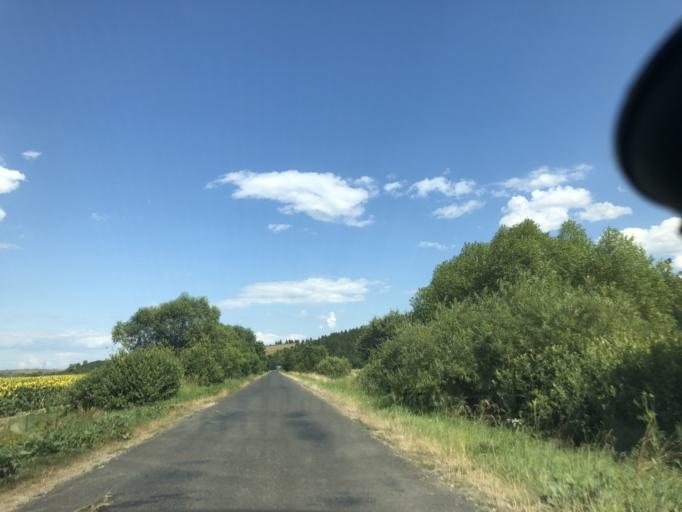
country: HU
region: Borsod-Abauj-Zemplen
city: Szendro
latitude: 48.5419
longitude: 20.7870
